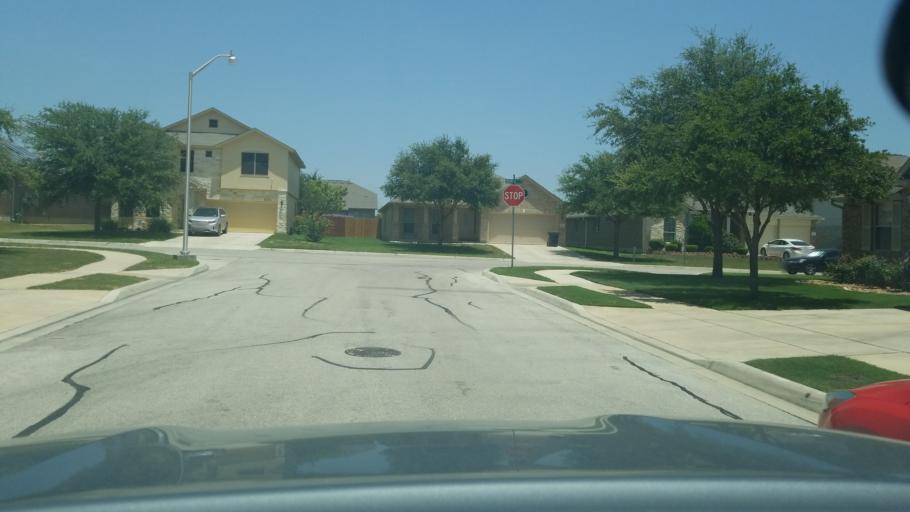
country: US
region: Texas
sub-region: Guadalupe County
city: Cibolo
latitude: 29.5774
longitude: -98.2300
